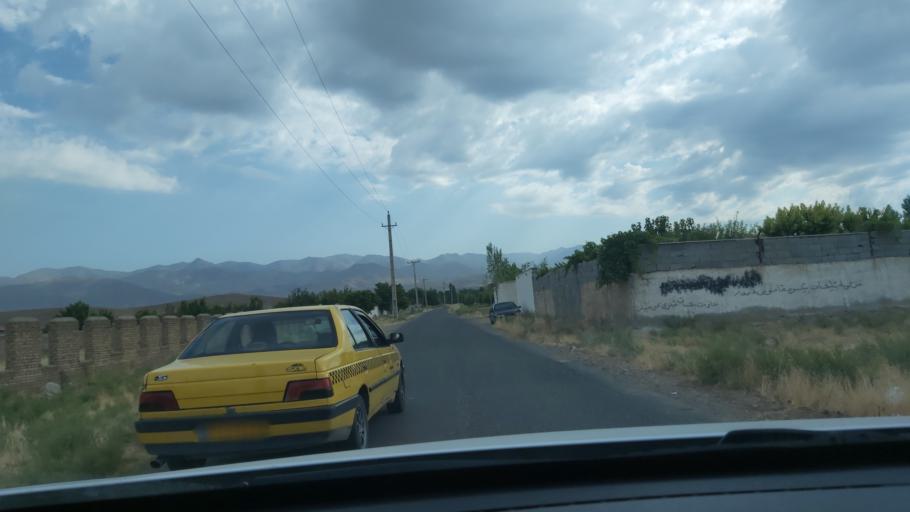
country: IR
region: Alborz
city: Hashtgerd
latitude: 35.9531
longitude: 50.7761
